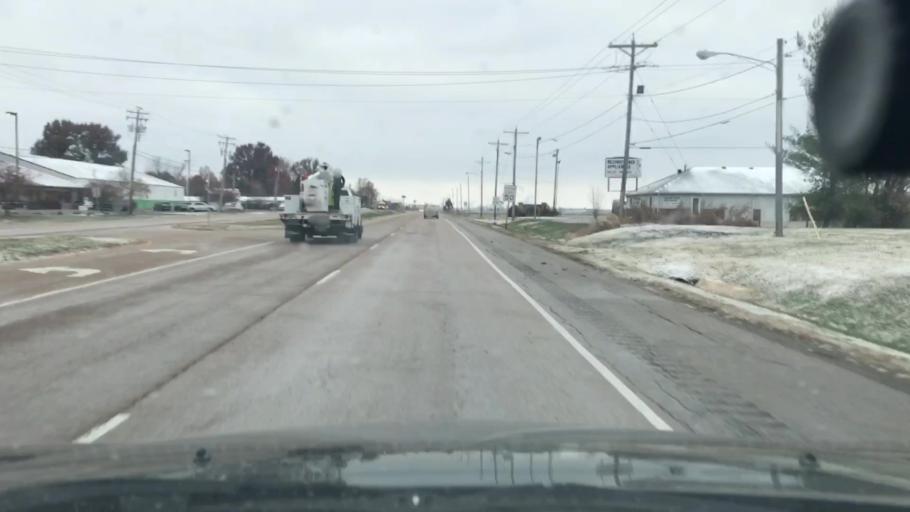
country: US
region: Illinois
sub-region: Madison County
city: Pontoon Beach
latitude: 38.7330
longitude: -90.0709
